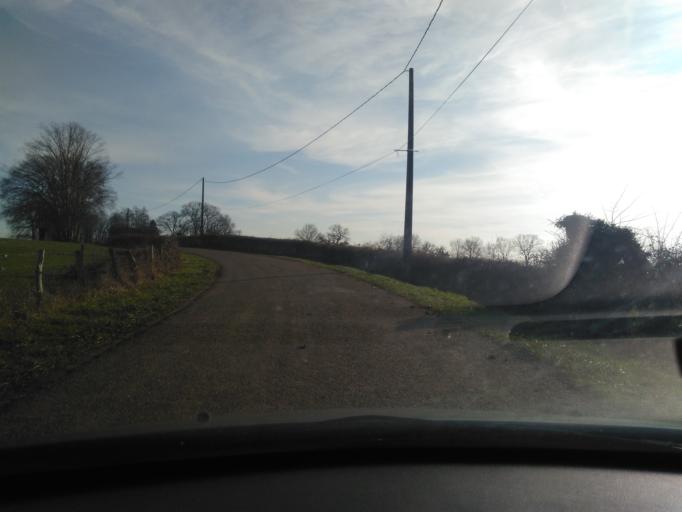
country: FR
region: Bourgogne
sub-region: Departement de la Nievre
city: Saint-Parize-le-Chatel
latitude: 46.8333
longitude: 3.2377
